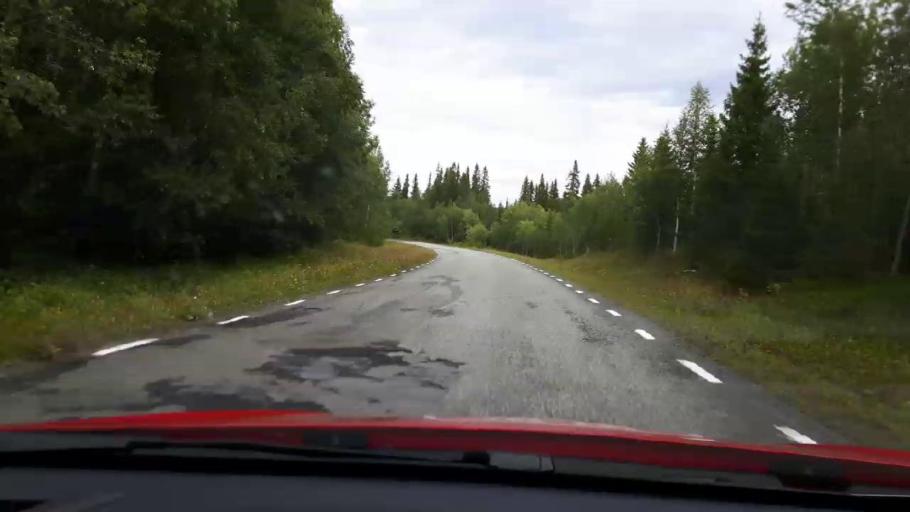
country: SE
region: Jaemtland
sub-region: Are Kommun
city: Are
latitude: 63.7169
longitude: 12.9665
